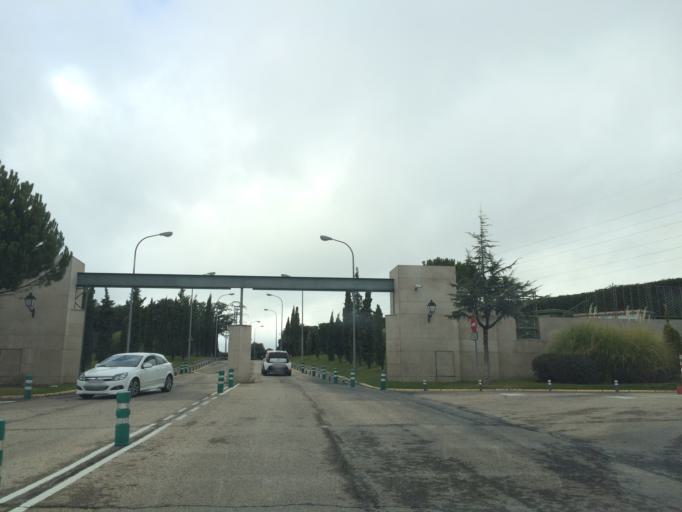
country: ES
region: Madrid
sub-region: Provincia de Madrid
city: Tres Cantos
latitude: 40.5780
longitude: -3.6991
